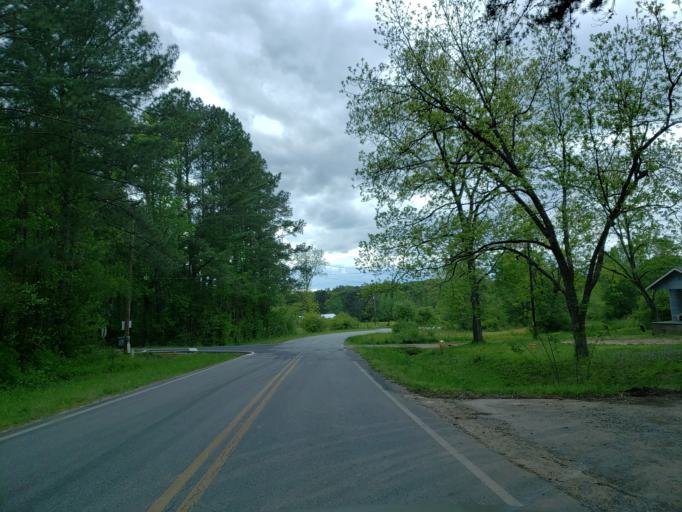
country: US
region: Georgia
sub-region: Haralson County
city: Tallapoosa
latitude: 33.7615
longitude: -85.3179
